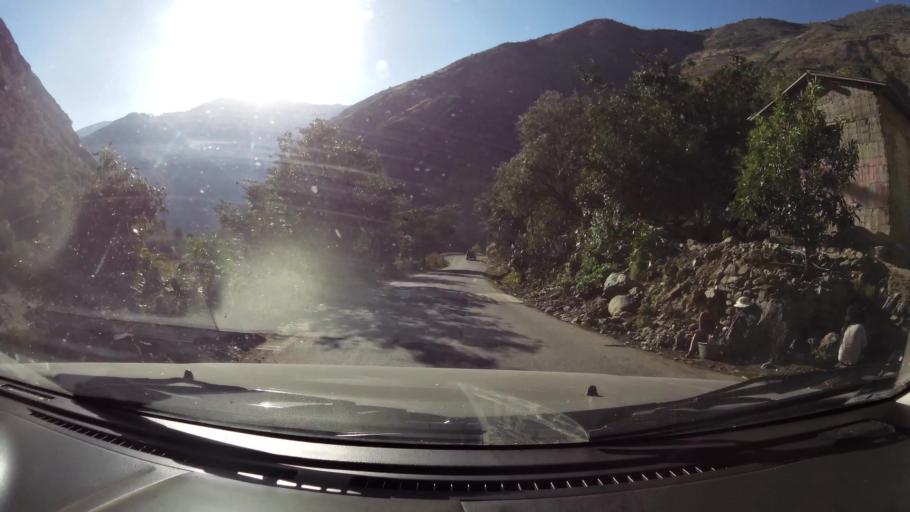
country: PE
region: Huancavelica
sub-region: Provincia de Churcampa
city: La Esmeralda
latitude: -12.5684
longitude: -74.6926
